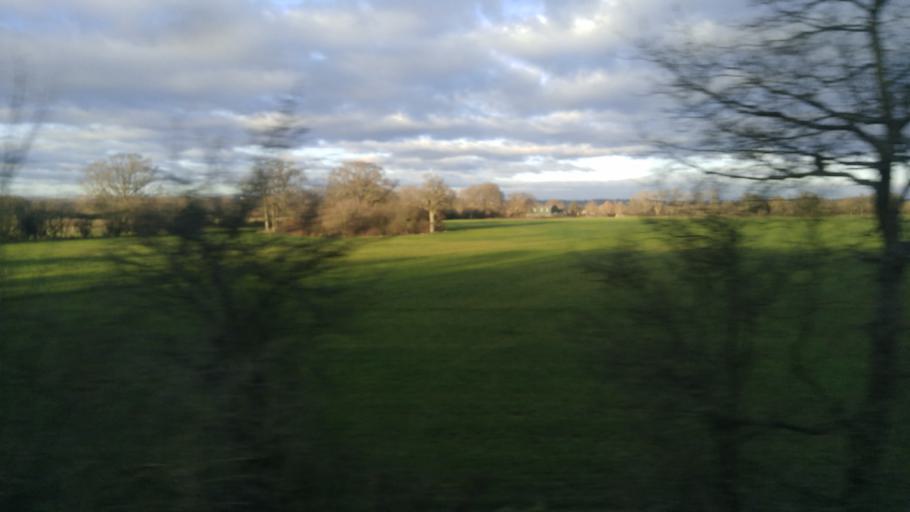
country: GB
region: England
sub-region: Kent
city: Headcorn
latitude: 51.1621
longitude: 0.6743
